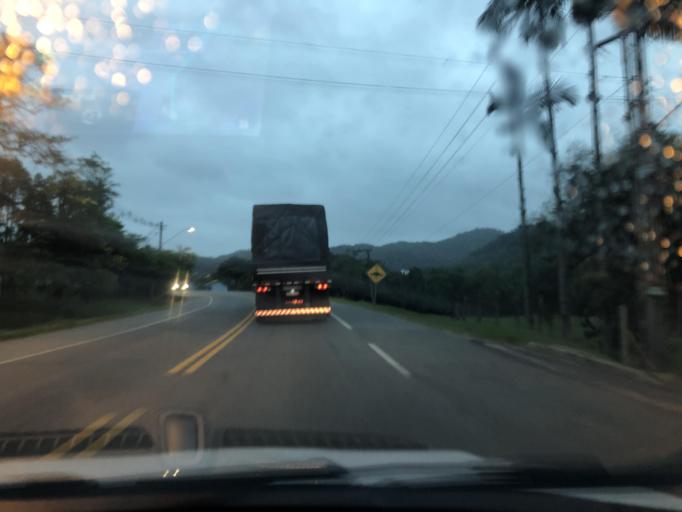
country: BR
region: Santa Catarina
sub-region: Pomerode
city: Pomerode
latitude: -26.7691
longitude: -49.0806
